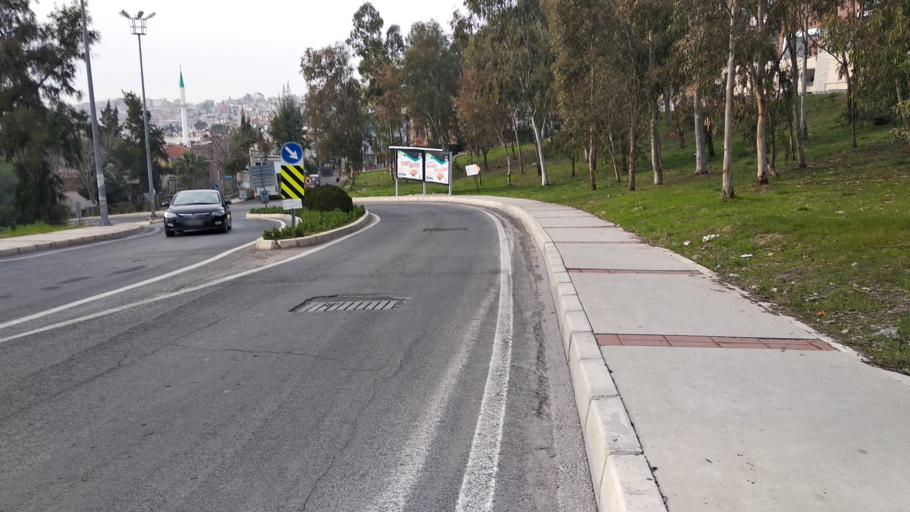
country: TR
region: Izmir
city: Karsiyaka
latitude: 38.4944
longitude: 27.0833
